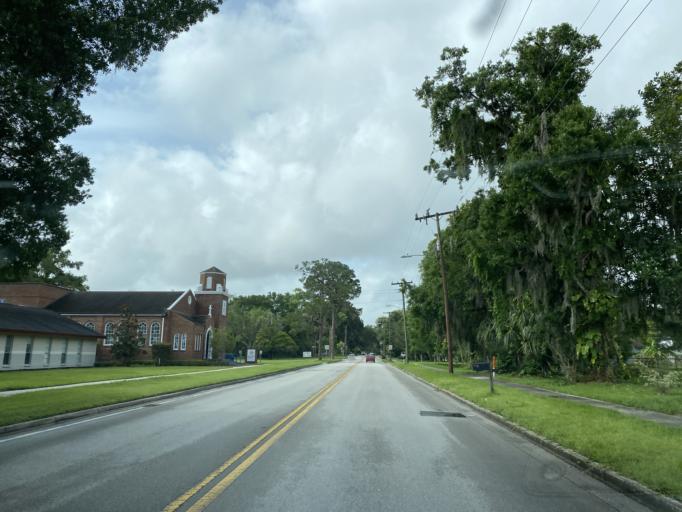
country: US
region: Florida
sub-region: Seminole County
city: Sanford
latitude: 28.7981
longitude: -81.2649
